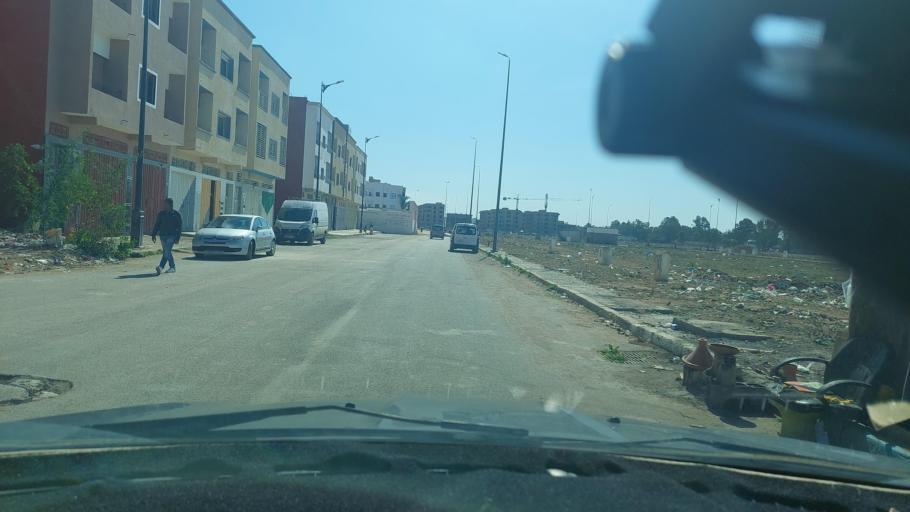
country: MA
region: Grand Casablanca
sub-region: Mediouna
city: Mediouna
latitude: 33.3802
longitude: -7.5376
